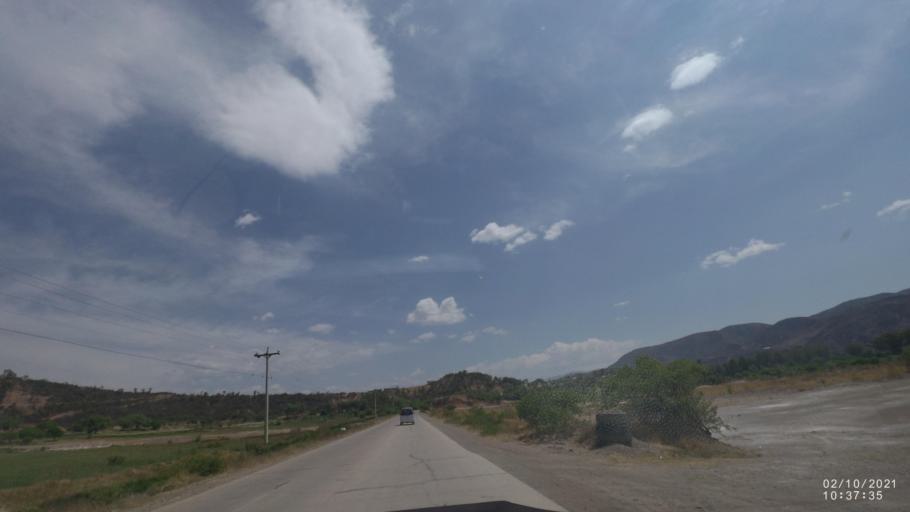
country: BO
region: Cochabamba
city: Capinota
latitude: -17.6420
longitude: -66.2652
